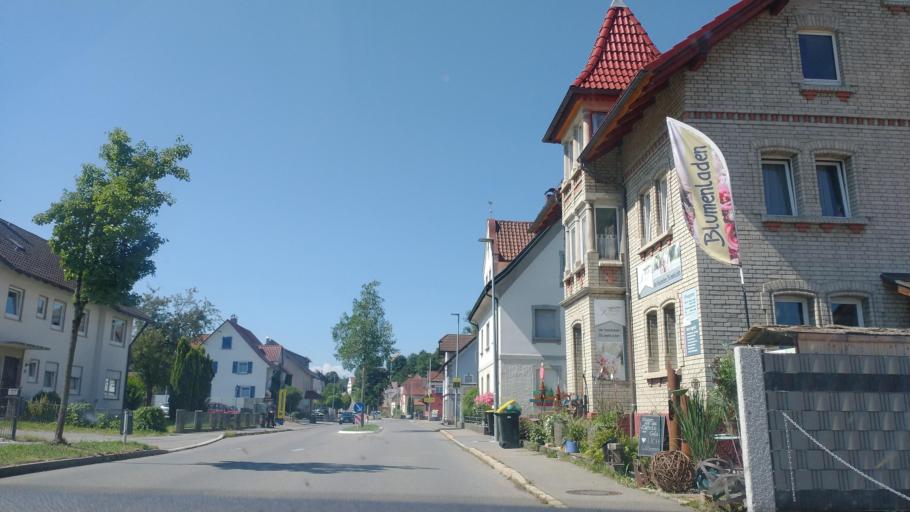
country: DE
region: Bavaria
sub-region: Swabia
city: Hergensweiler
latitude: 47.6407
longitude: 9.7617
